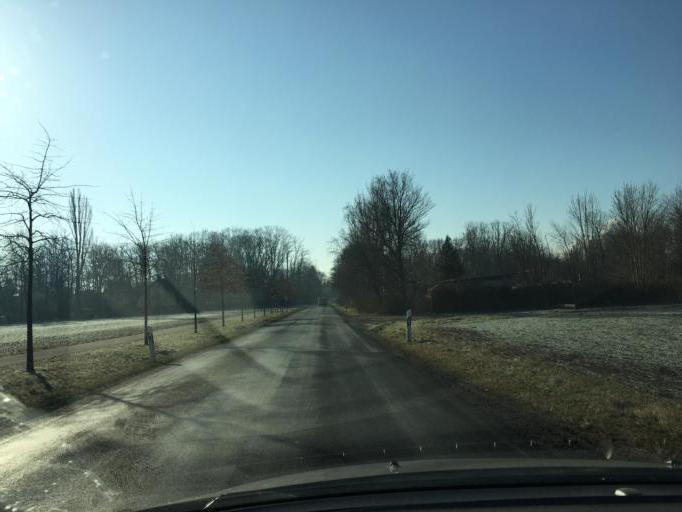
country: DE
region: Saxony
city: Grossposna
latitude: 51.3187
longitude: 12.4519
